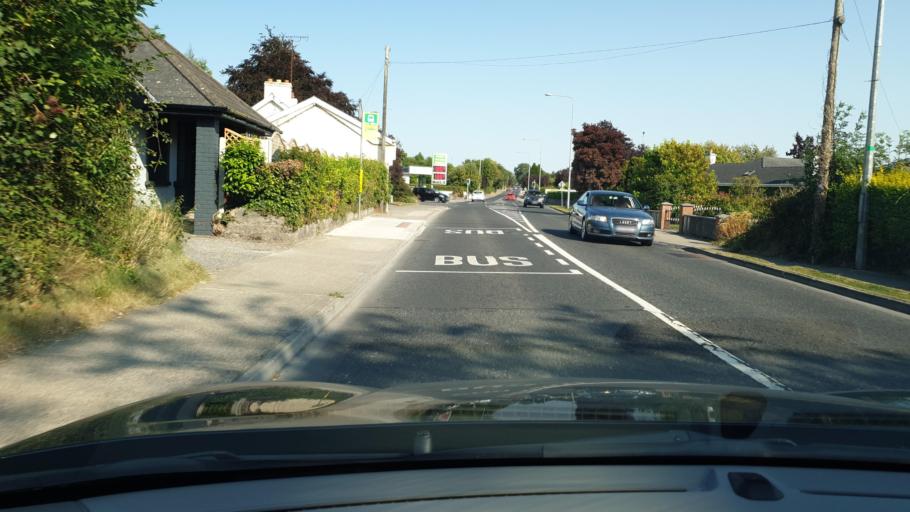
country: IE
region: Leinster
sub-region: An Mhi
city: Navan
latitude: 53.6508
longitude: -6.6660
